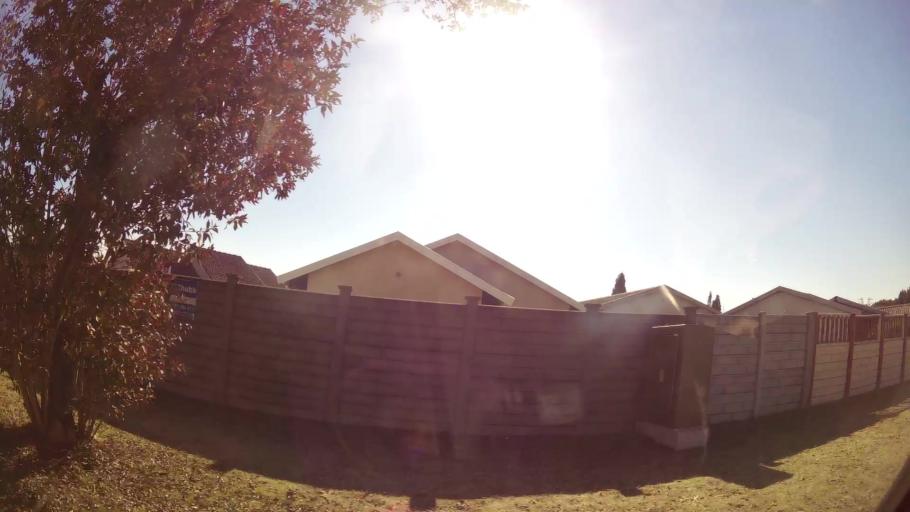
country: ZA
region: Gauteng
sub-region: City of Johannesburg Metropolitan Municipality
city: Johannesburg
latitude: -26.2417
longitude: 28.1023
